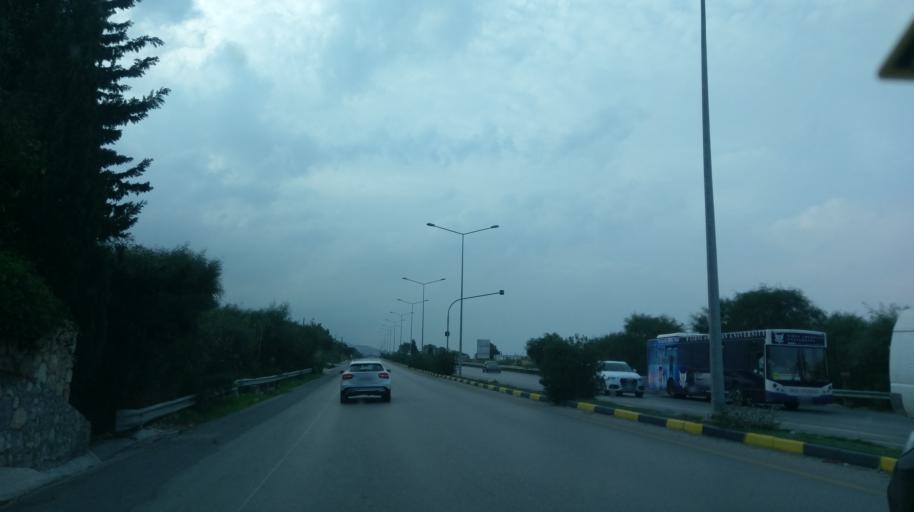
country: CY
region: Keryneia
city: Kyrenia
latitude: 35.3280
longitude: 33.2974
